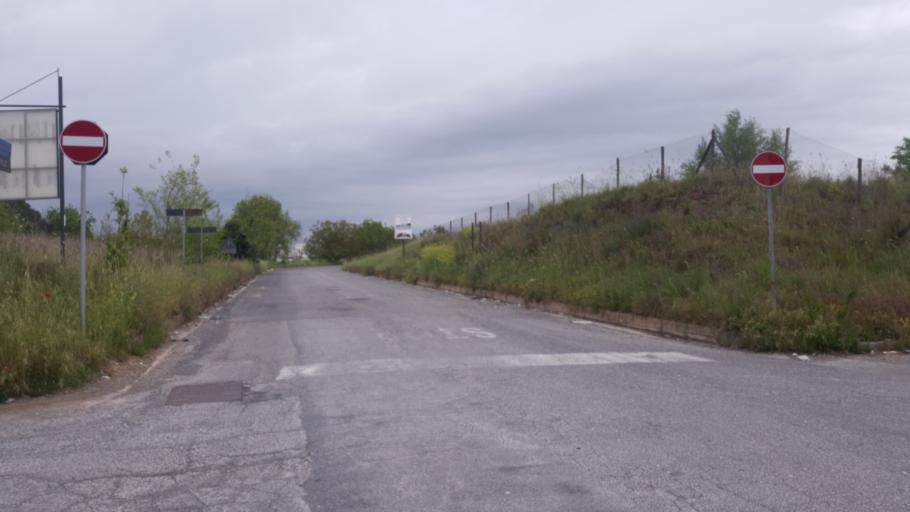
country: IT
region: Latium
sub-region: Citta metropolitana di Roma Capitale
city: Setteville
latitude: 41.9309
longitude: 12.6091
